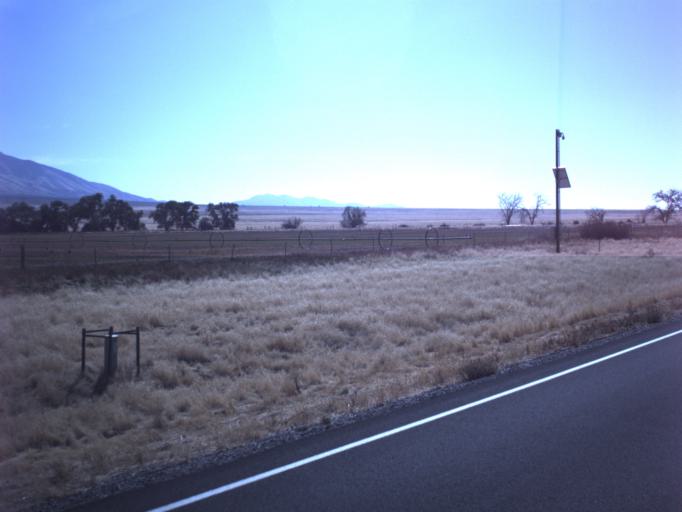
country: US
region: Utah
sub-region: Tooele County
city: Grantsville
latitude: 40.4575
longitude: -112.7476
